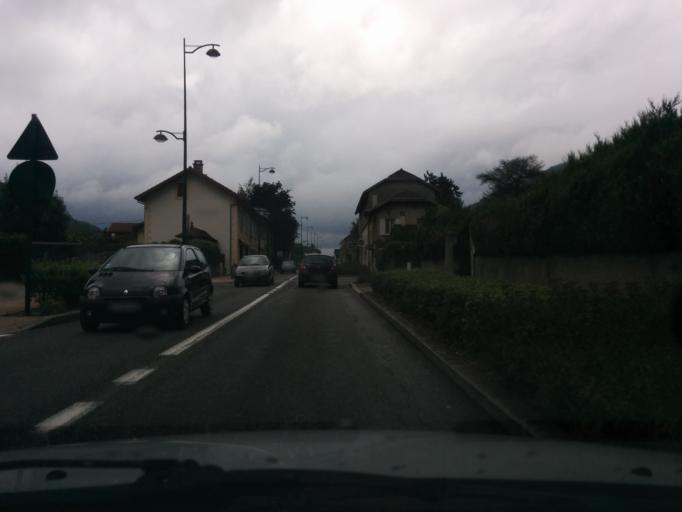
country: FR
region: Rhone-Alpes
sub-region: Departement de l'Isere
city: Chirens
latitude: 45.4145
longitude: 5.5560
